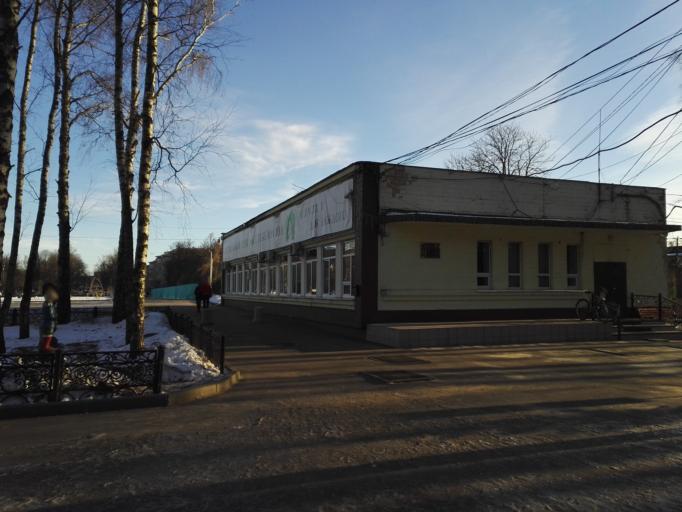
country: RU
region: Tula
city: Tula
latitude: 54.1776
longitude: 37.5929
